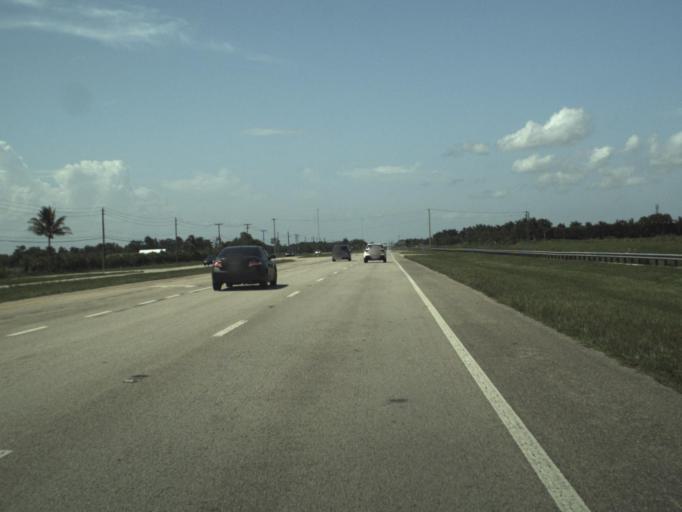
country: US
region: Florida
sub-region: Palm Beach County
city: Villages of Oriole
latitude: 26.5094
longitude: -80.2051
